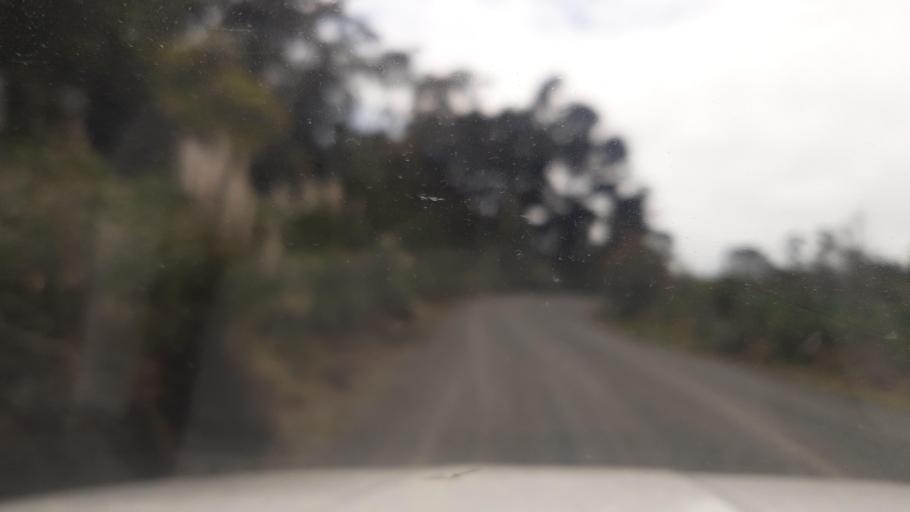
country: NZ
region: Northland
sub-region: Far North District
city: Kaitaia
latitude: -34.8361
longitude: 173.1207
